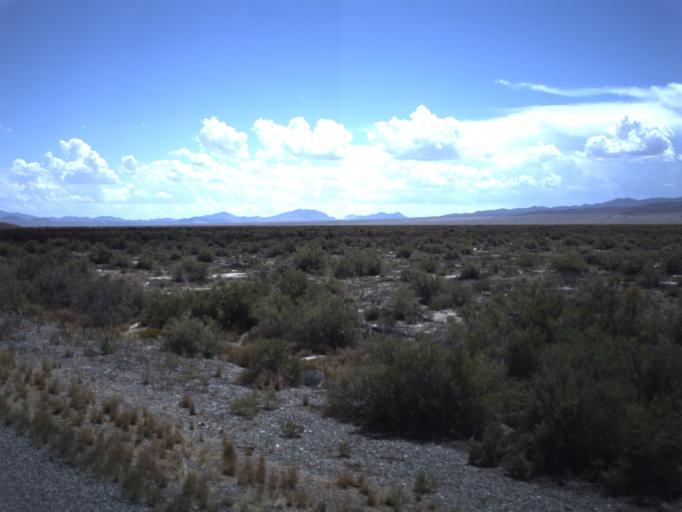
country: US
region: Nevada
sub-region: White Pine County
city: McGill
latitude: 39.0492
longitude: -113.9455
